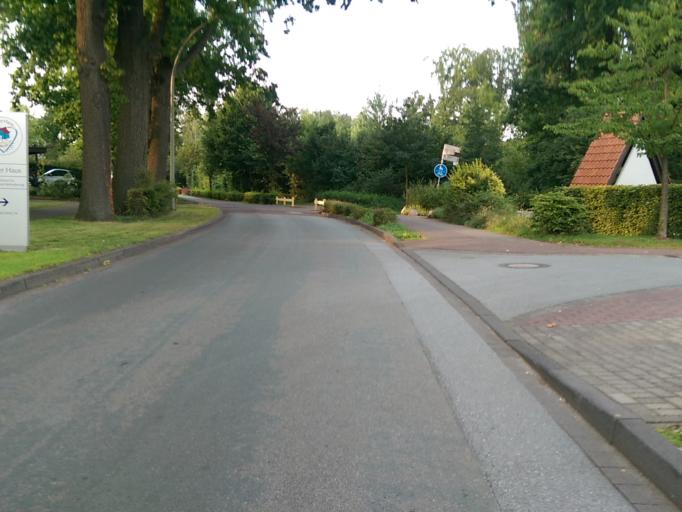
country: DE
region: North Rhine-Westphalia
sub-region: Regierungsbezirk Detmold
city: Rheda-Wiedenbruck
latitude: 51.8849
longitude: 8.2343
